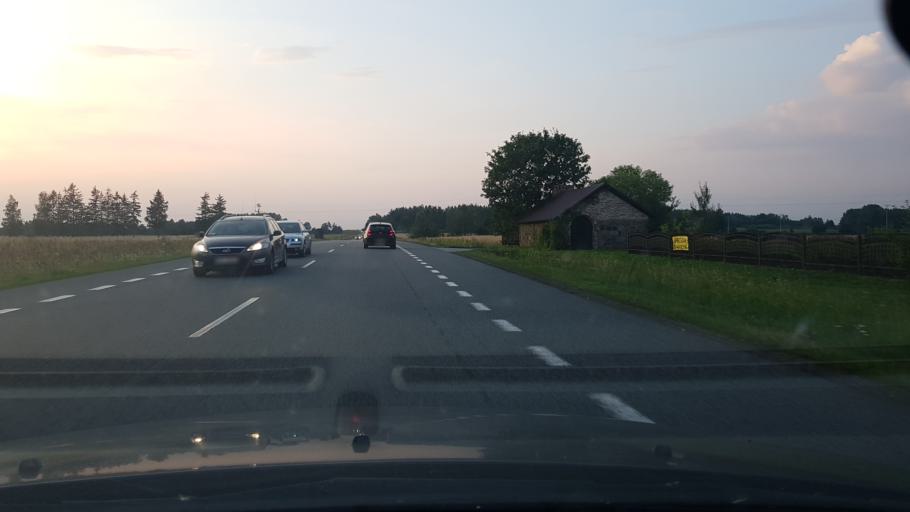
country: PL
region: Masovian Voivodeship
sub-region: Powiat mlawski
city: Wieczfnia Koscielna
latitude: 53.2029
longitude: 20.4350
